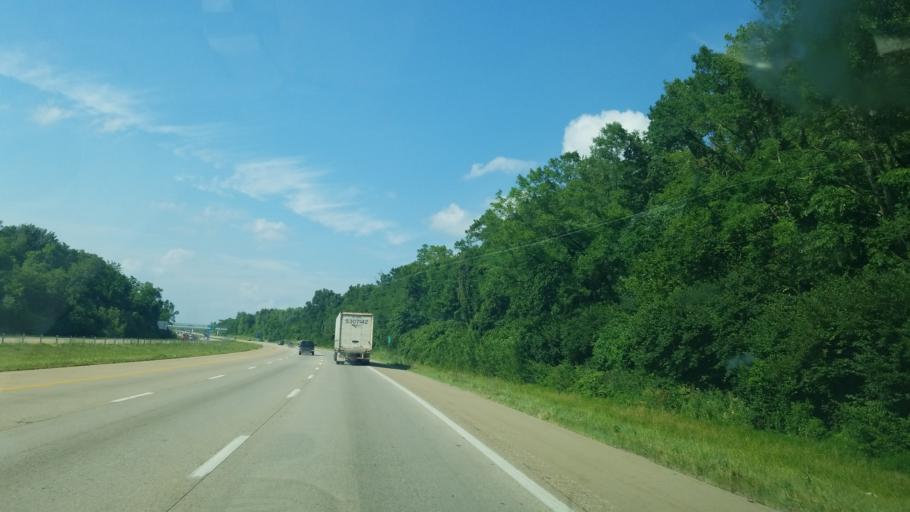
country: US
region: Ohio
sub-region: Clermont County
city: Withamsville
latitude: 39.0779
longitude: -84.2915
